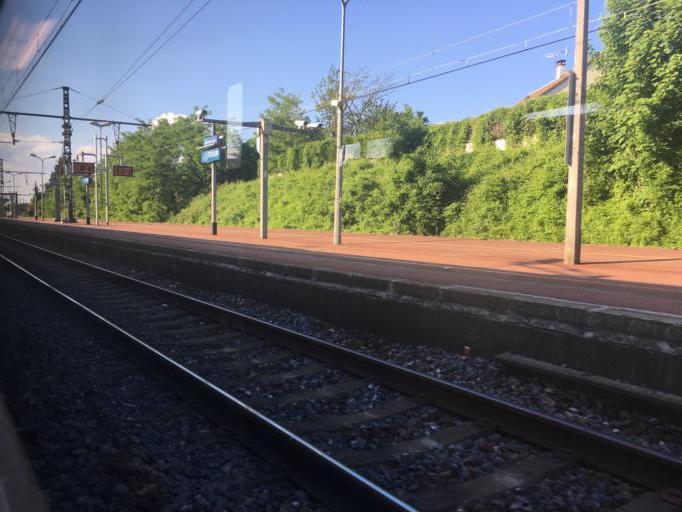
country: FR
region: Ile-de-France
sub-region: Departement de Seine-et-Marne
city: Cesson
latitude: 48.5639
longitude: 2.5952
